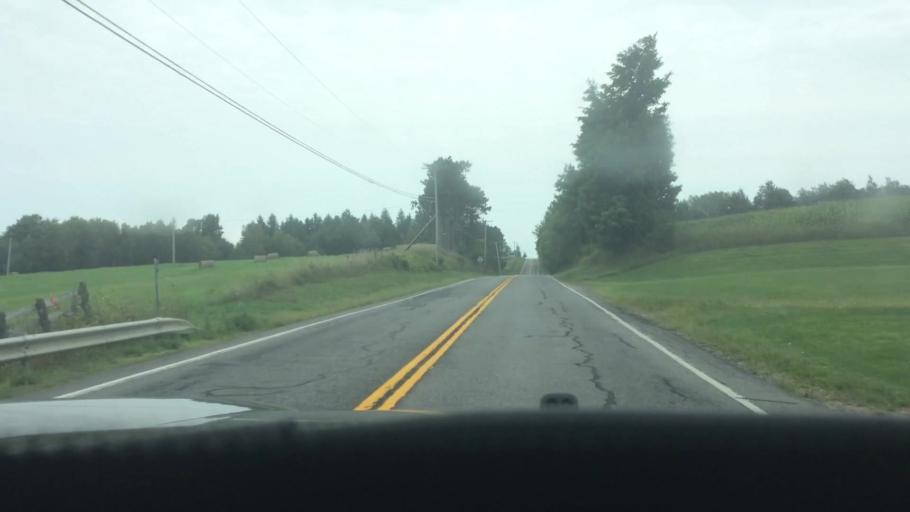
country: US
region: New York
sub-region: St. Lawrence County
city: Hannawa Falls
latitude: 44.6763
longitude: -74.7246
